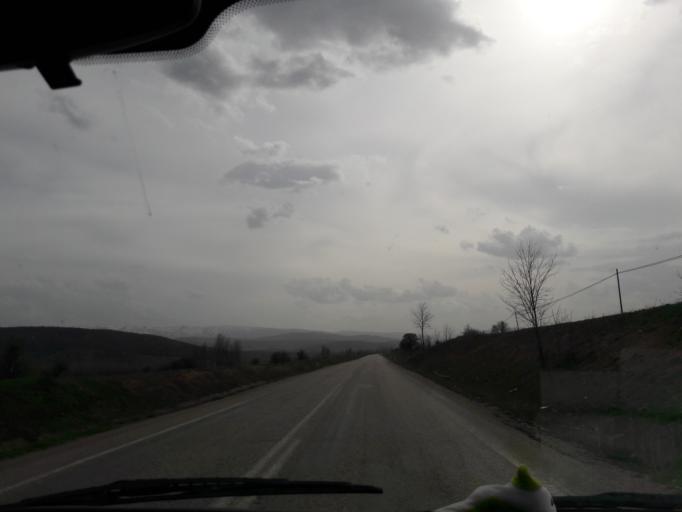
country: TR
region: Gumushane
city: Siran
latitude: 40.1755
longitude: 39.0879
